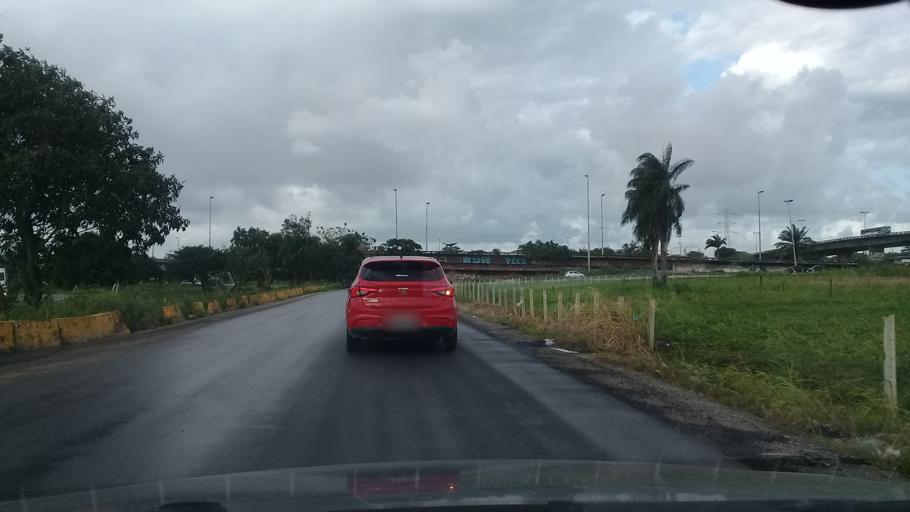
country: BR
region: Pernambuco
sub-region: Recife
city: Recife
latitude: -8.0662
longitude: -34.9450
